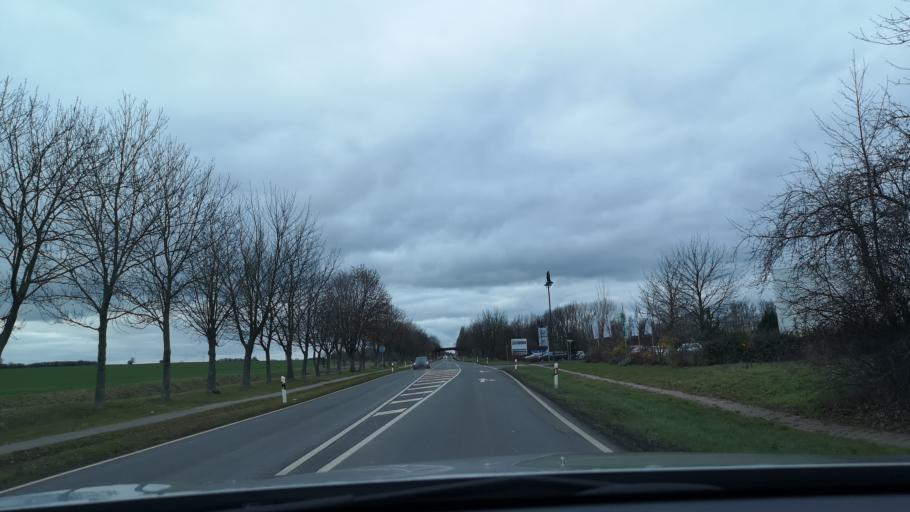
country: DE
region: Saxony-Anhalt
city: Braunsbedra
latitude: 51.2844
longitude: 11.8721
